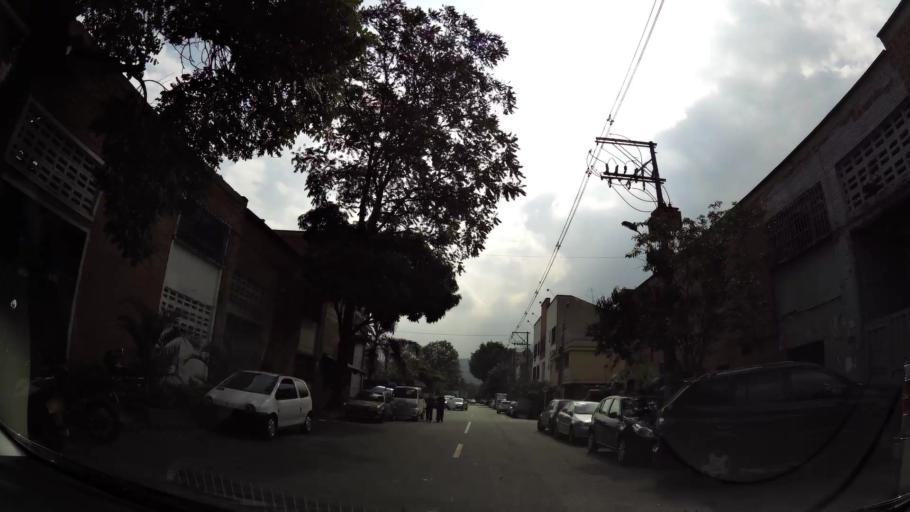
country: CO
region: Antioquia
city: Medellin
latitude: 6.2306
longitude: -75.5809
